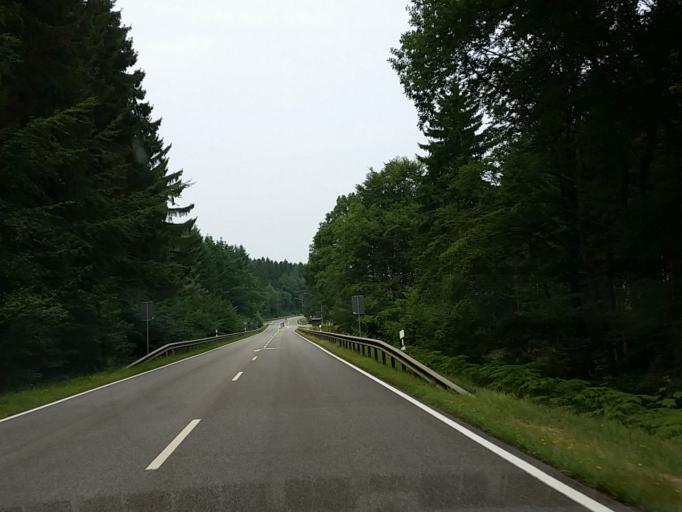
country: DE
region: Rheinland-Pfalz
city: Farschweiler
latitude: 49.7104
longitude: 6.8244
